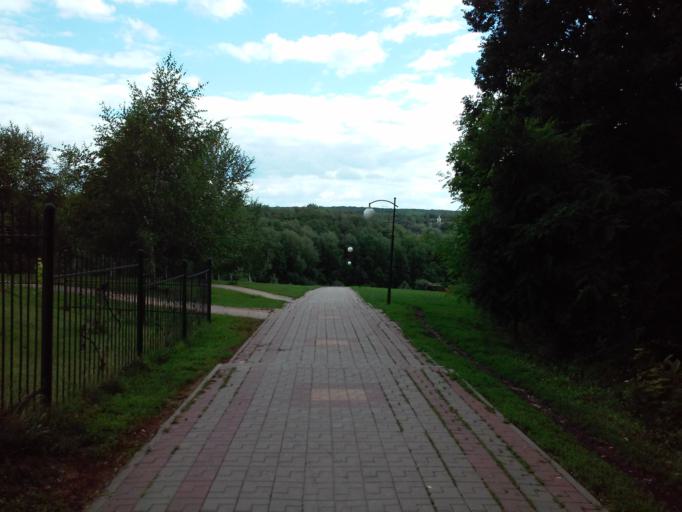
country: RU
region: Belgorod
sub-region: Belgorodskiy Rayon
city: Belgorod
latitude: 50.5360
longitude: 36.5843
